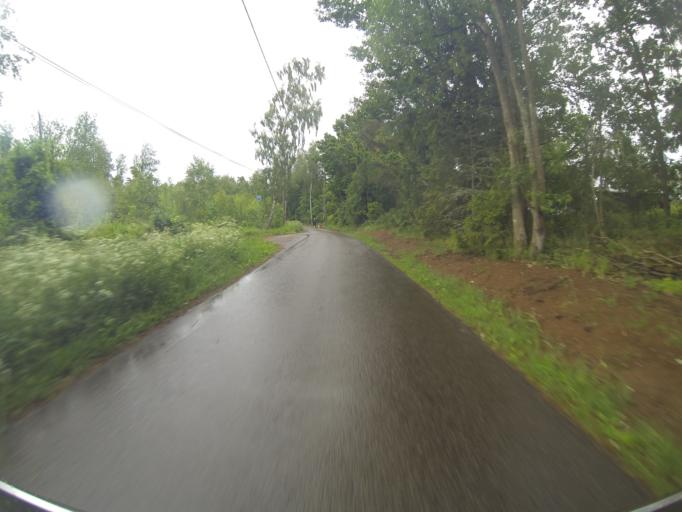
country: SE
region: Blekinge
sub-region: Ronneby Kommun
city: Ronneby
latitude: 56.1708
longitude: 15.3114
